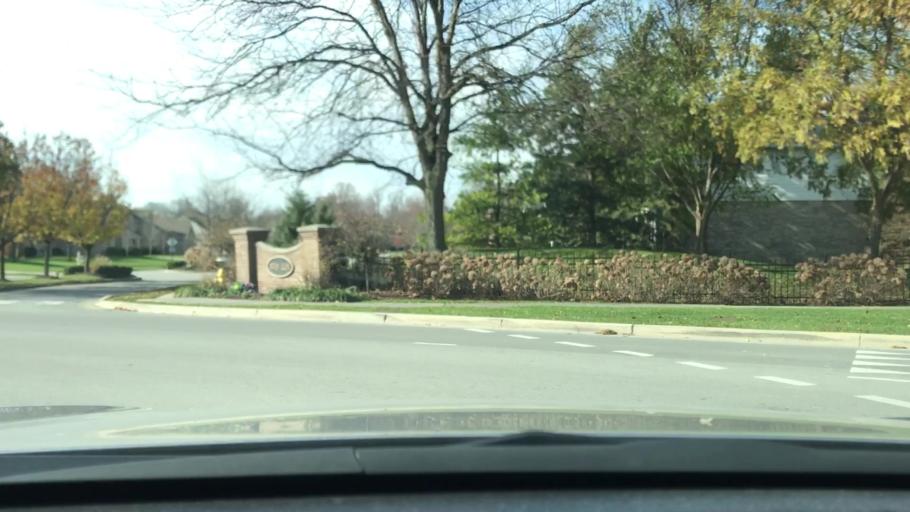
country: US
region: Indiana
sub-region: Hamilton County
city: Carmel
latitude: 39.9924
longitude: -86.0705
